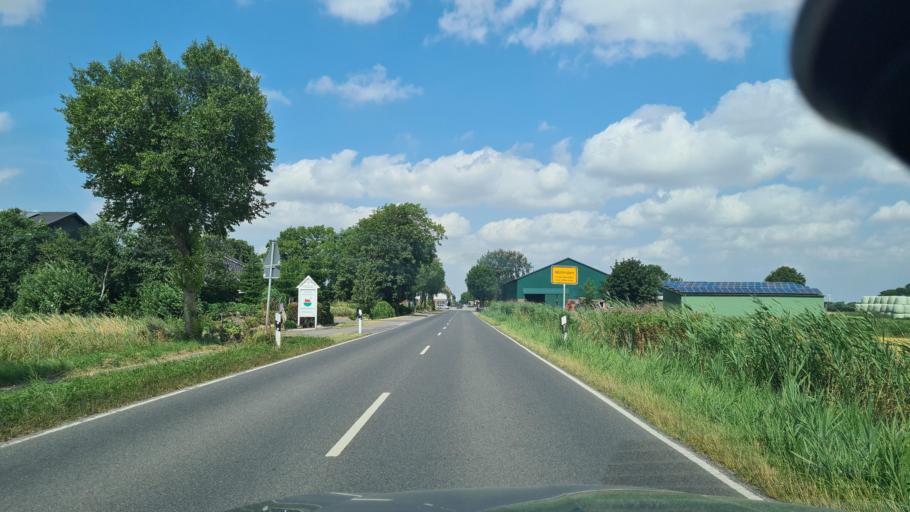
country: DE
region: Schleswig-Holstein
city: Wohrden
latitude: 54.1421
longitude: 9.0166
